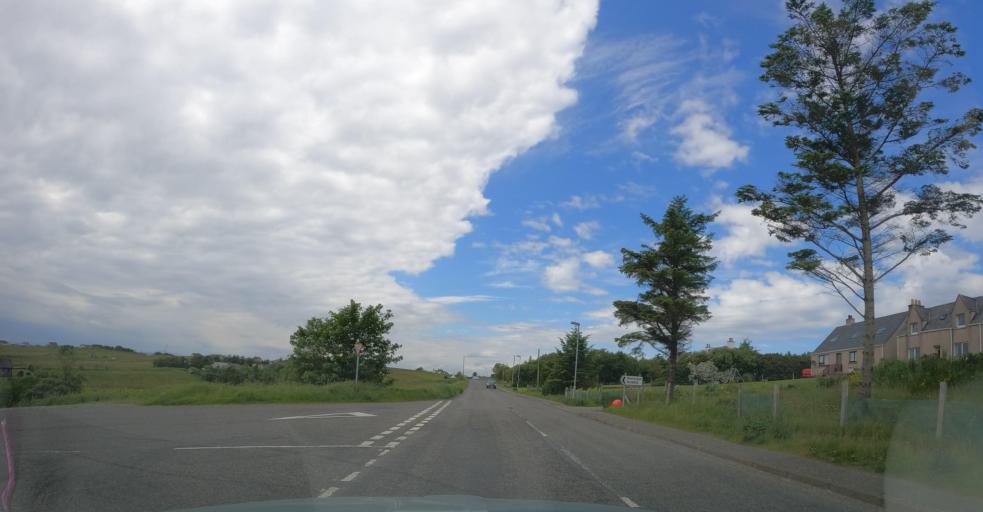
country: GB
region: Scotland
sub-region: Eilean Siar
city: Isle of Lewis
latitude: 58.2762
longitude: -6.2990
